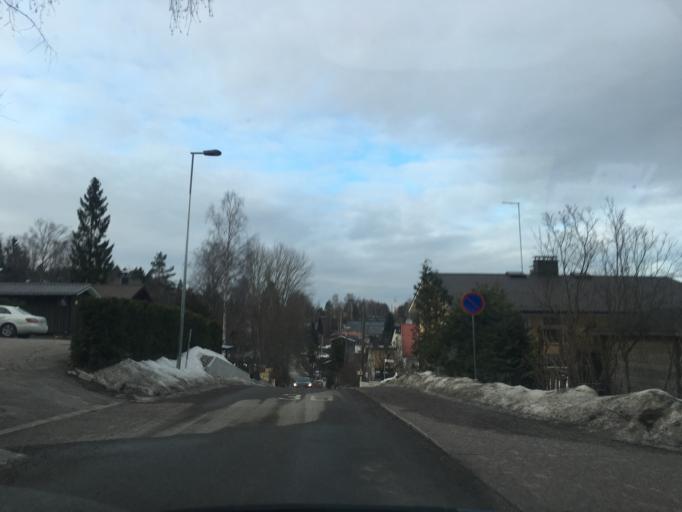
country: FI
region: Uusimaa
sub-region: Helsinki
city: Vantaa
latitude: 60.2645
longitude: 25.0889
